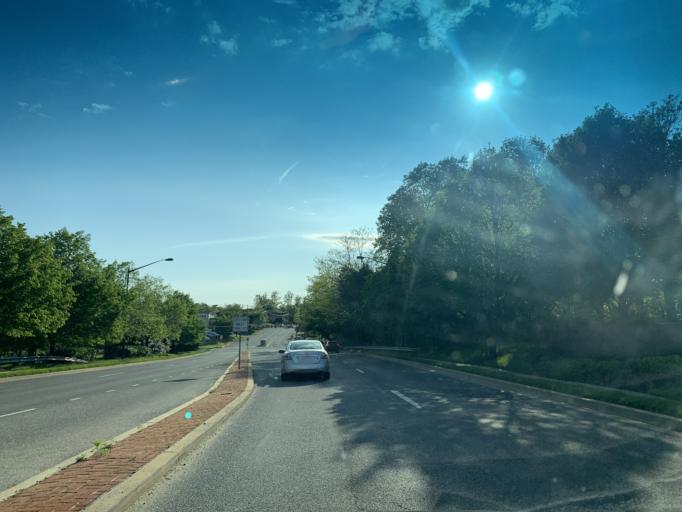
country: US
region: Maryland
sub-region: Anne Arundel County
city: Parole
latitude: 38.9917
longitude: -76.5480
